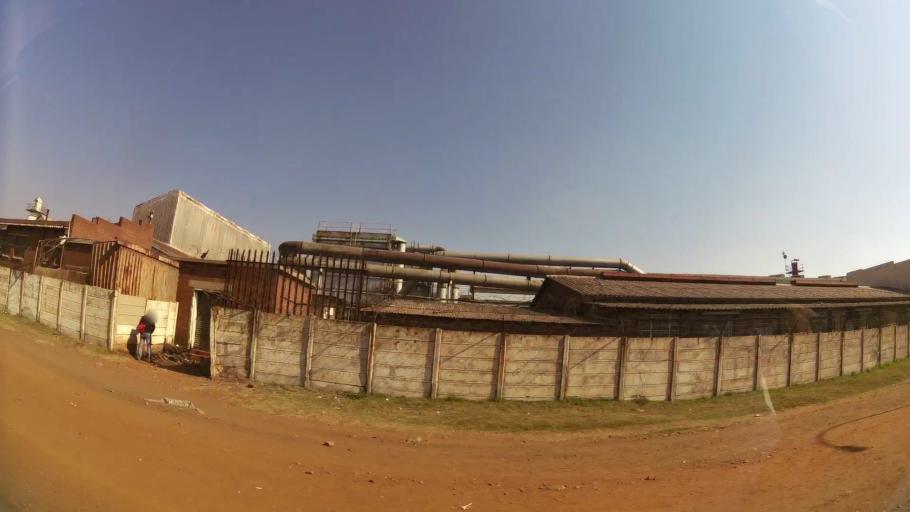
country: ZA
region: Gauteng
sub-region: Ekurhuleni Metropolitan Municipality
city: Benoni
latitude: -26.2094
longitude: 28.2940
